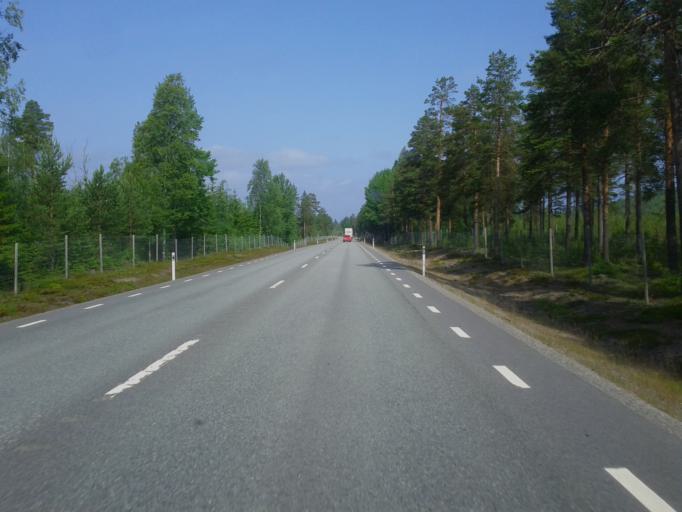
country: SE
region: Vaesterbotten
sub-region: Skelleftea Kommun
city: Burea
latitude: 64.5807
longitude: 21.2211
